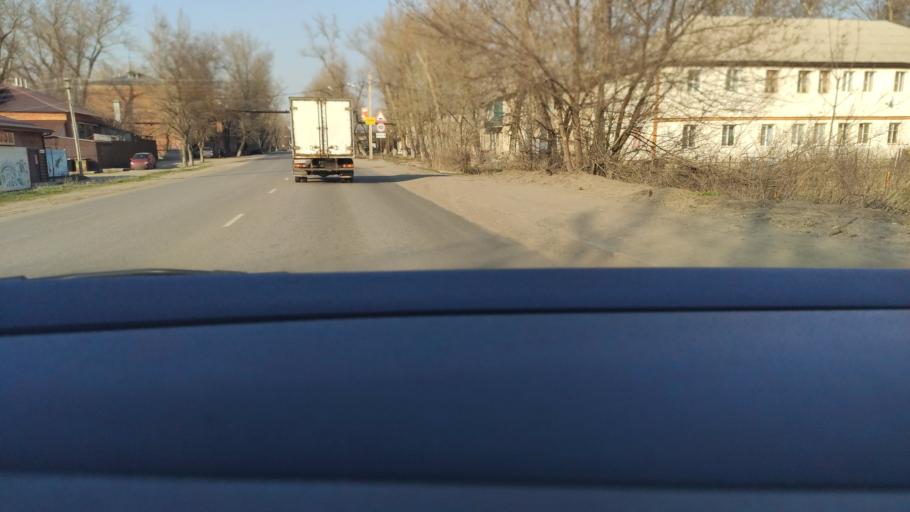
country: RU
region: Voronezj
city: Maslovka
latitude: 51.5792
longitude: 39.3143
